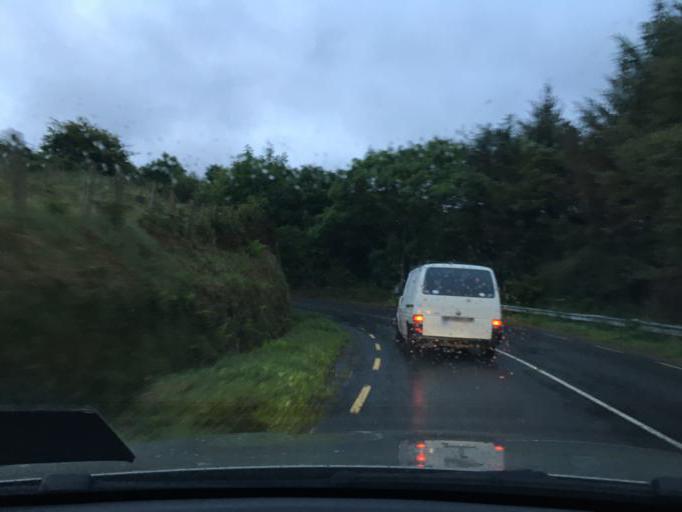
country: IE
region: Ulster
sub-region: County Donegal
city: Killybegs
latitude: 54.6352
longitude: -8.4737
